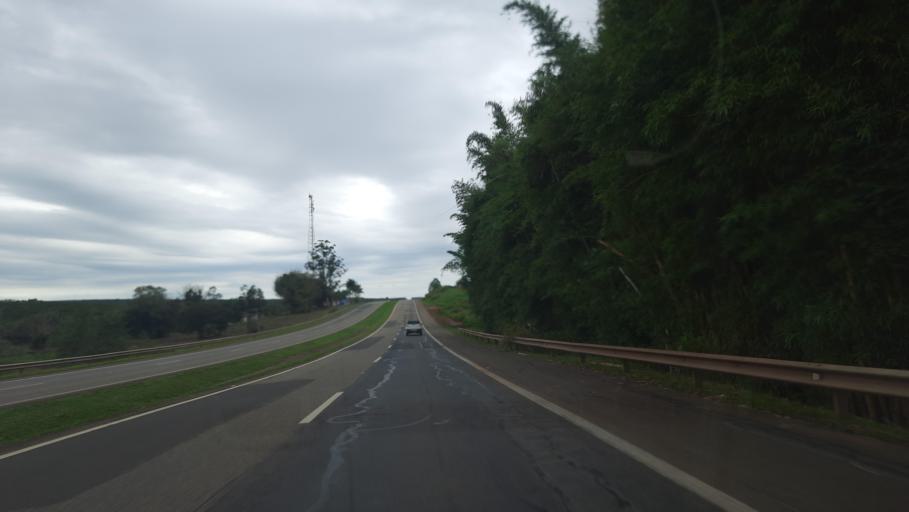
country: BR
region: Sao Paulo
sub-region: Casa Branca
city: Casa Branca
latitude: -21.8338
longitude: -47.0674
